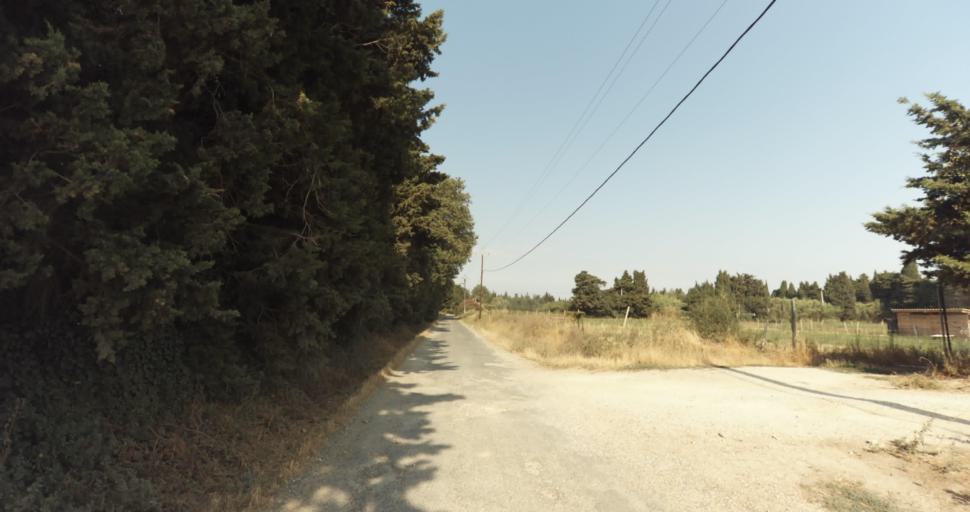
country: FR
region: Languedoc-Roussillon
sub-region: Departement des Pyrenees-Orientales
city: Latour-Bas-Elne
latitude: 42.6008
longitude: 3.0117
